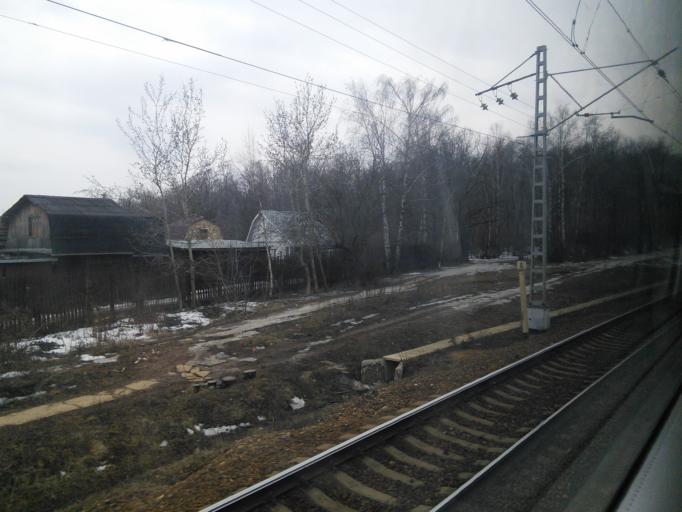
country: RU
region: Moskovskaya
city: Vostryakovo
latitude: 55.4165
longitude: 37.8256
